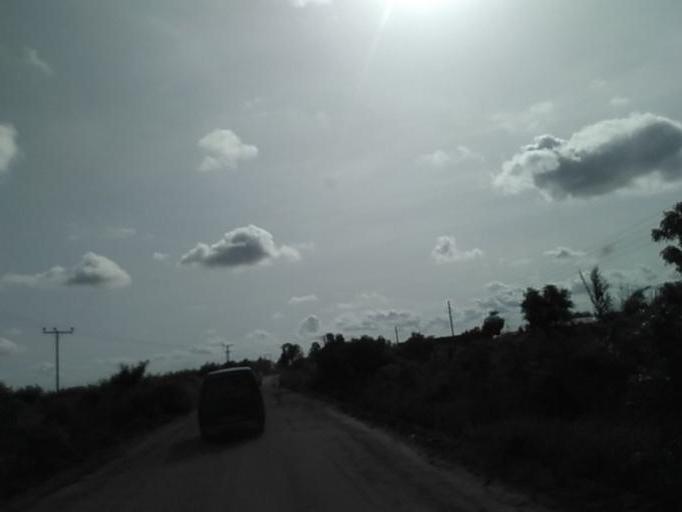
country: GH
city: Akropong
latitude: 6.0319
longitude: 0.3426
